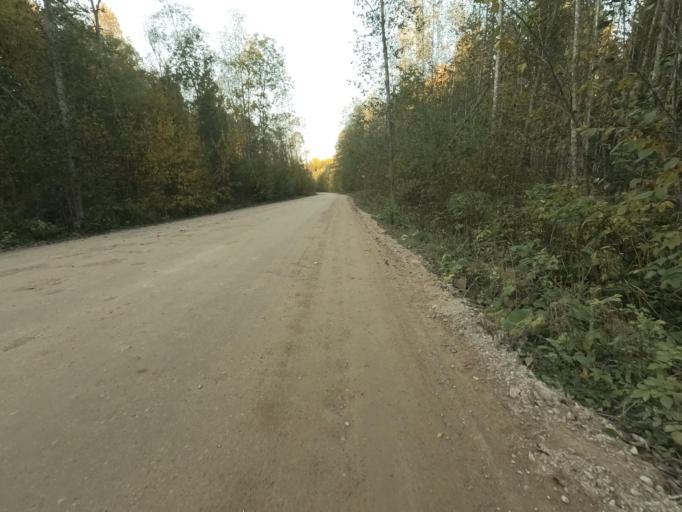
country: RU
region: Leningrad
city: Lyuban'
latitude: 58.9944
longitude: 31.1059
